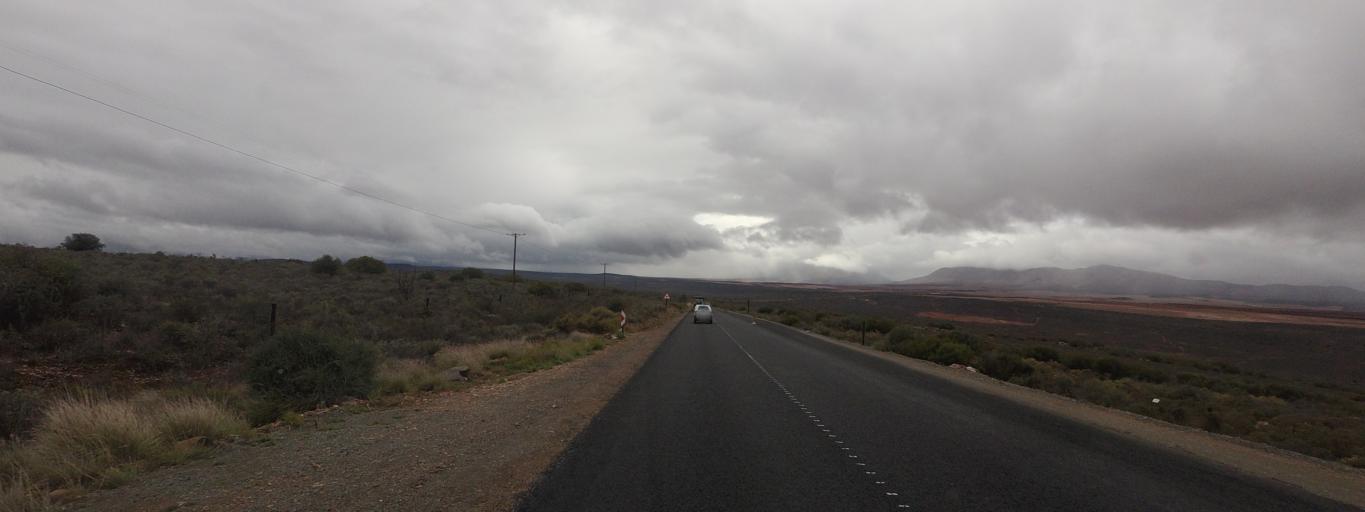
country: ZA
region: Western Cape
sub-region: Eden District Municipality
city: Oudtshoorn
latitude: -33.7292
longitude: 22.3077
